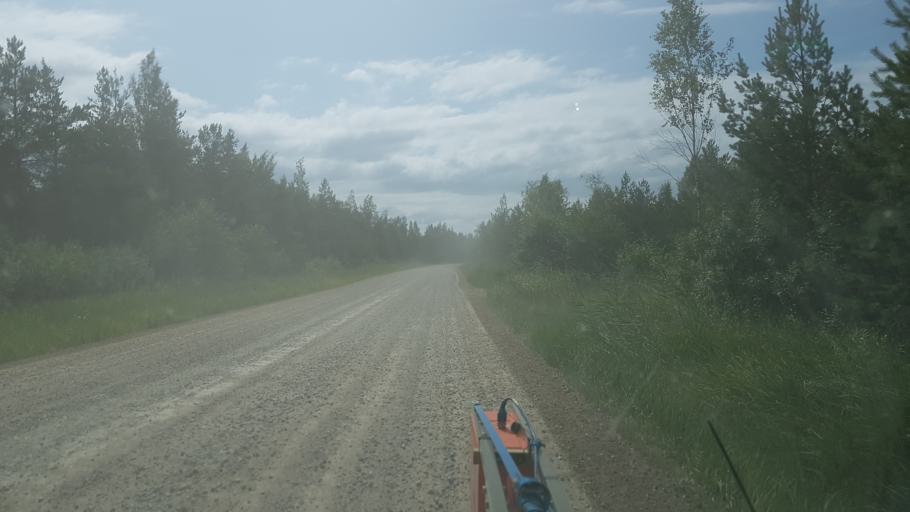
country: EE
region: Paernumaa
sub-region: Audru vald
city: Audru
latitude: 58.5278
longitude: 24.4068
